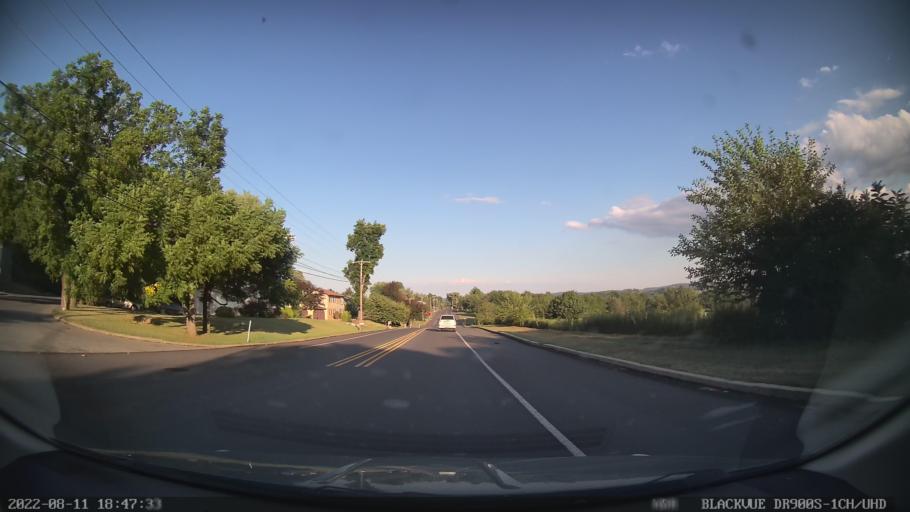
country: US
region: Pennsylvania
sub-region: Lehigh County
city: Wescosville
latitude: 40.5858
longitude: -75.5487
